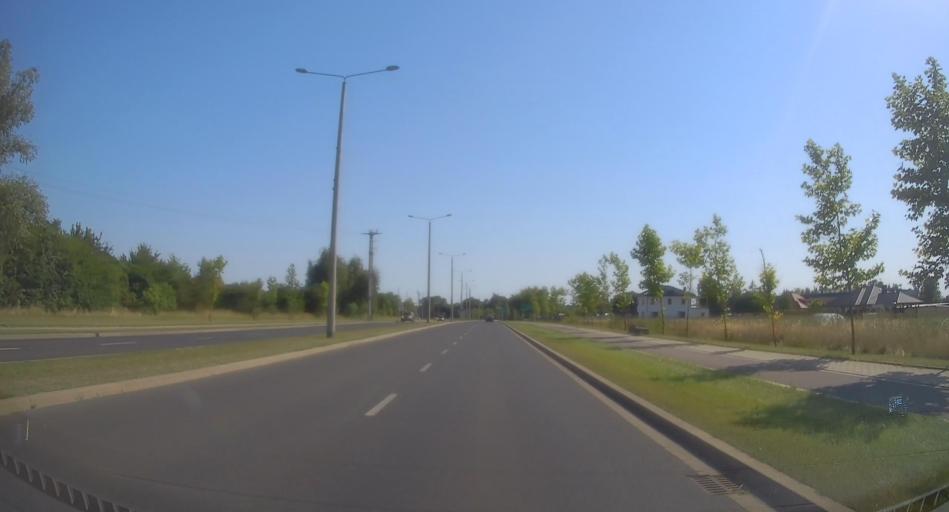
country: PL
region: Lodz Voivodeship
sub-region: Skierniewice
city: Skierniewice
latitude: 51.9461
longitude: 20.1586
